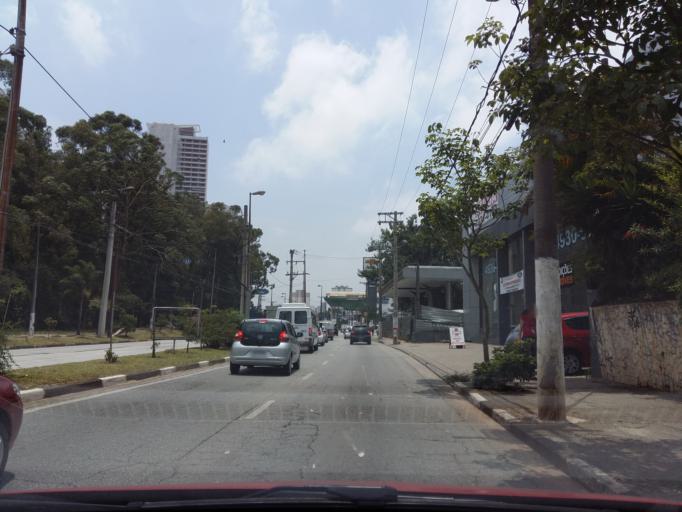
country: BR
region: Sao Paulo
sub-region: Sao Bernardo Do Campo
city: Sao Bernardo do Campo
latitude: -23.6889
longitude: -46.5478
